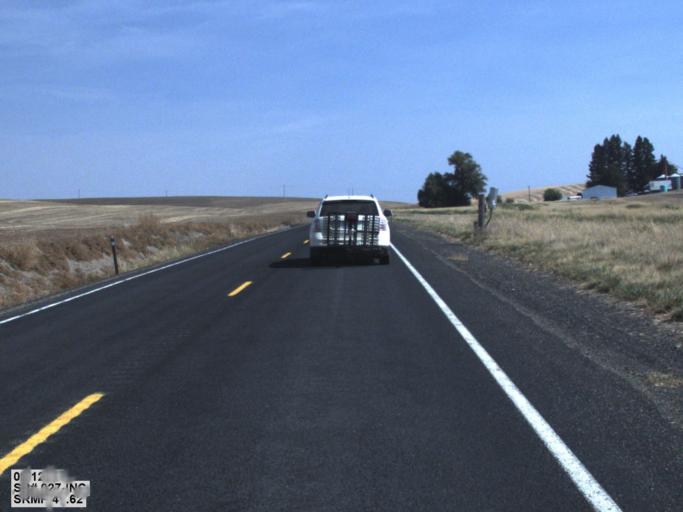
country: US
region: Idaho
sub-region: Benewah County
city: Plummer
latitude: 47.1797
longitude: -117.1800
